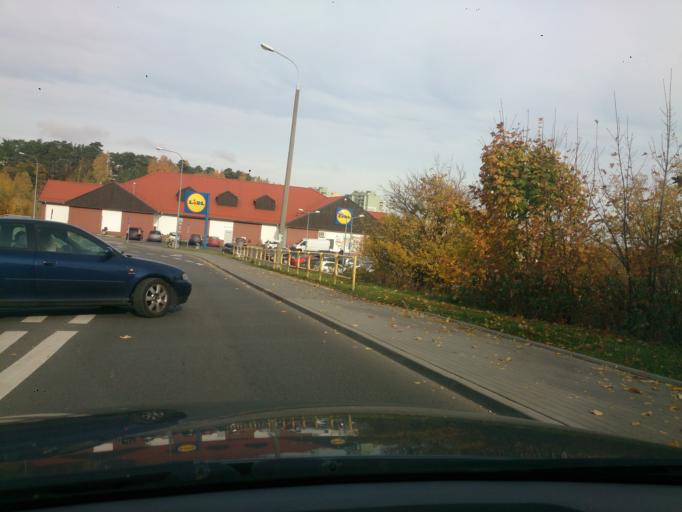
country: PL
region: Pomeranian Voivodeship
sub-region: Gdynia
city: Wielki Kack
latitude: 54.4691
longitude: 18.4915
